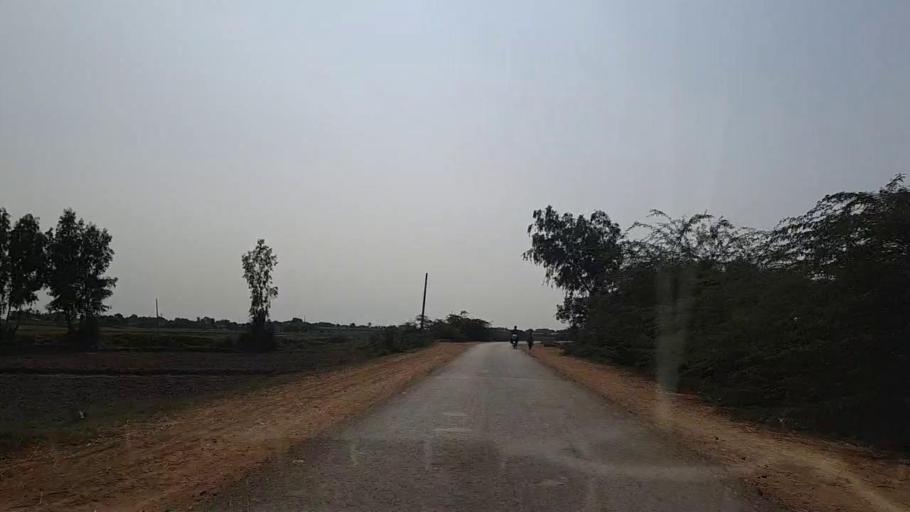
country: PK
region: Sindh
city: Chuhar Jamali
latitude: 24.3107
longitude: 67.9389
